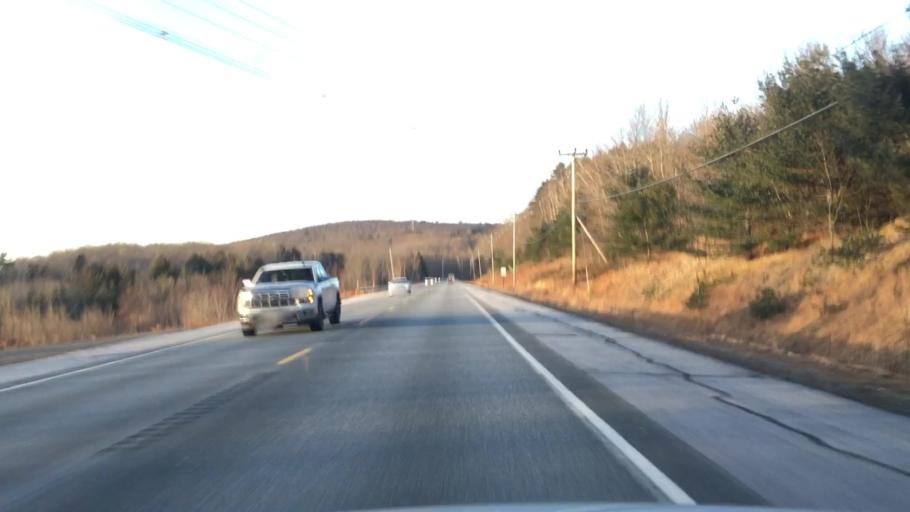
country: US
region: Maine
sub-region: Hancock County
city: Dedham
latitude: 44.7109
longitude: -68.6029
